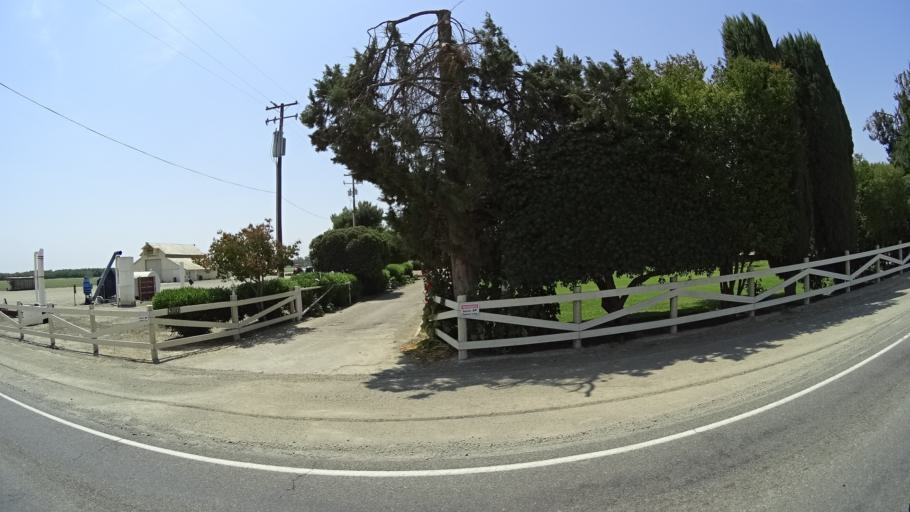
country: US
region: California
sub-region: Kings County
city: Lemoore
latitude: 36.3280
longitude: -119.7990
